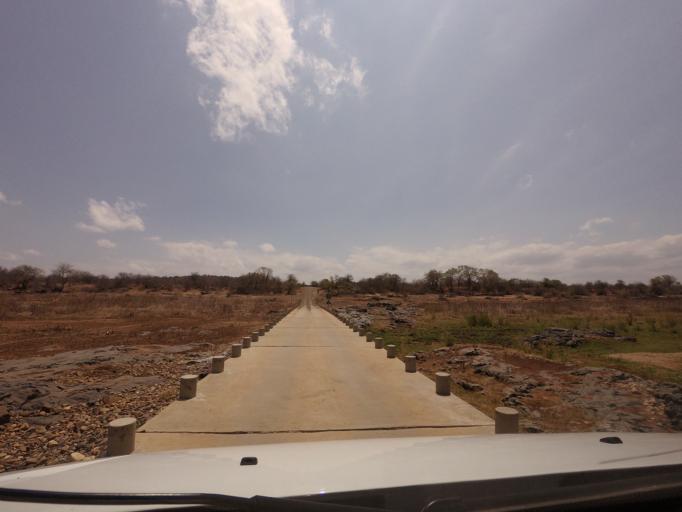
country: ZA
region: Limpopo
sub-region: Mopani District Municipality
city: Phalaborwa
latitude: -24.0522
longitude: 31.7296
